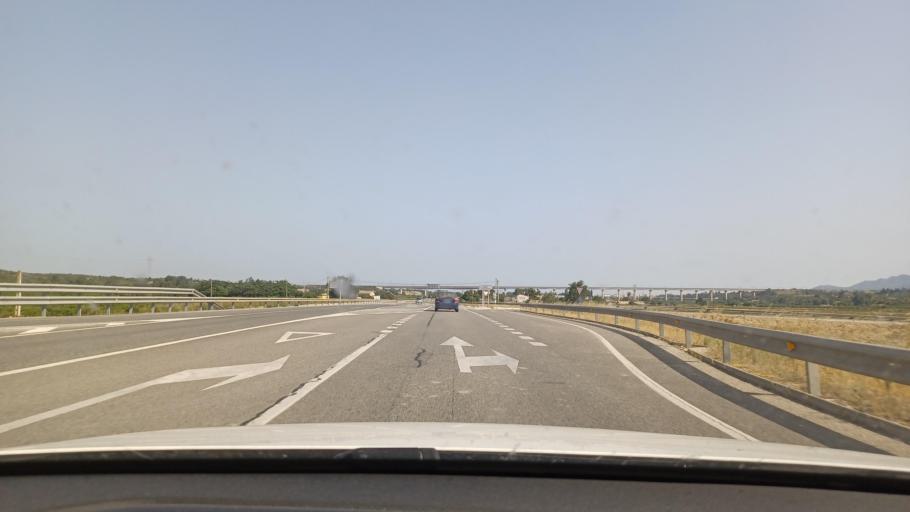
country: ES
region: Catalonia
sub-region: Provincia de Tarragona
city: Amposta
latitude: 40.7427
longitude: 0.5628
